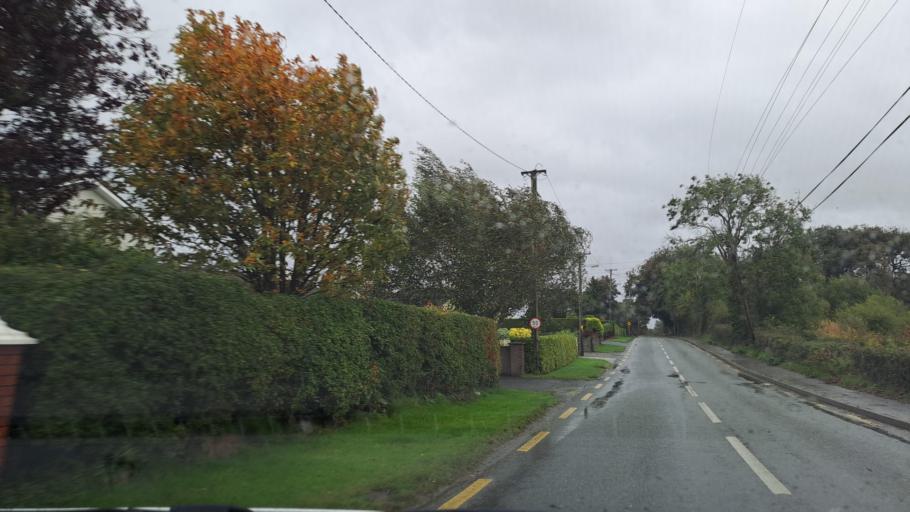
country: IE
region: Leinster
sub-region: Lu
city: Dundalk
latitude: 53.9694
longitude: -6.4814
